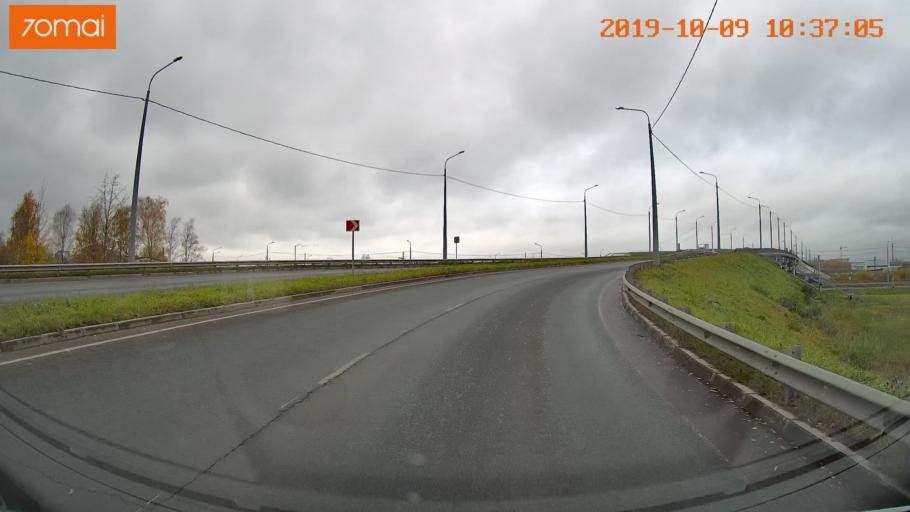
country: RU
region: Vologda
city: Vologda
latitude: 59.2338
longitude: 39.8683
